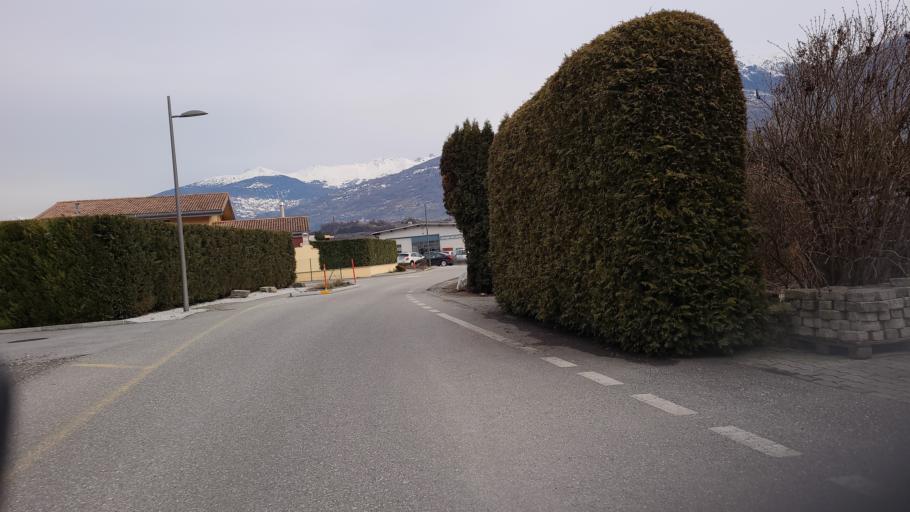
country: CH
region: Valais
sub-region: Conthey District
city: Vetroz
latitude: 46.2230
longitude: 7.2898
